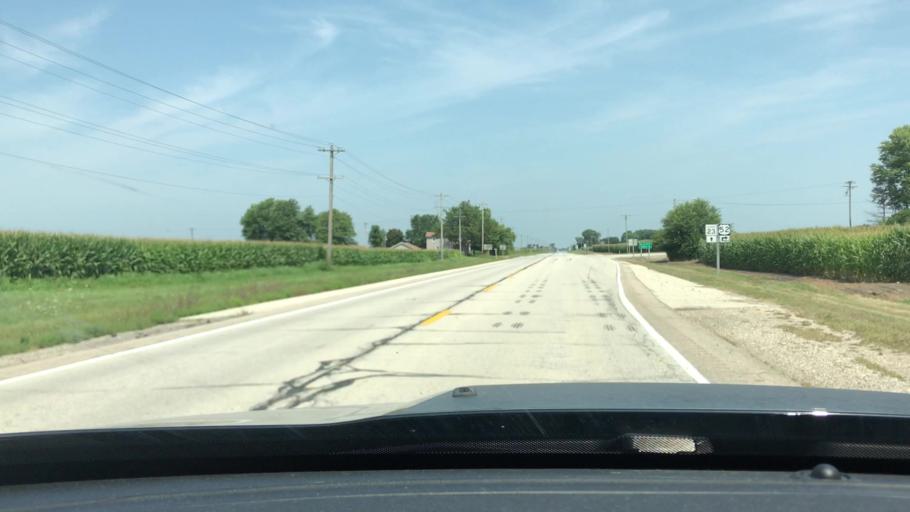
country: US
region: Illinois
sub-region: LaSalle County
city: Ottawa
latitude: 41.4838
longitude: -88.8151
